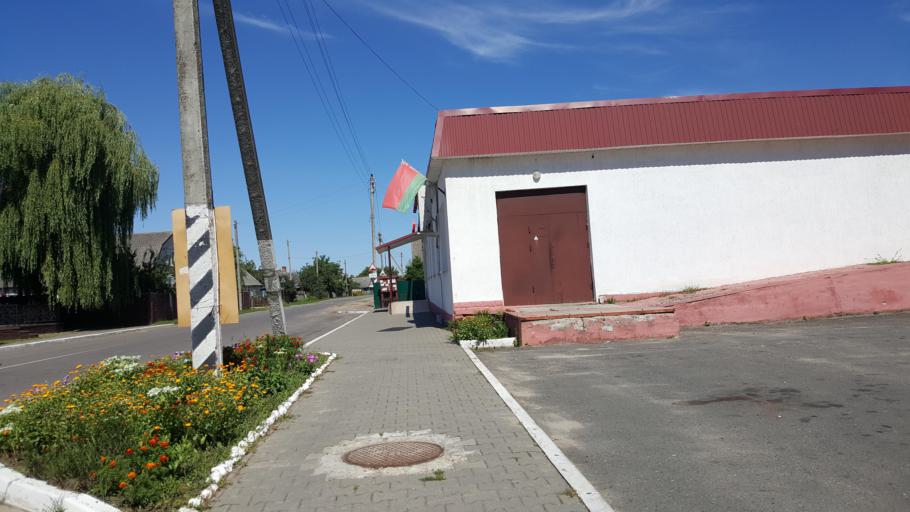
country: BY
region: Brest
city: Charnawchytsy
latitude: 52.2209
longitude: 23.7394
